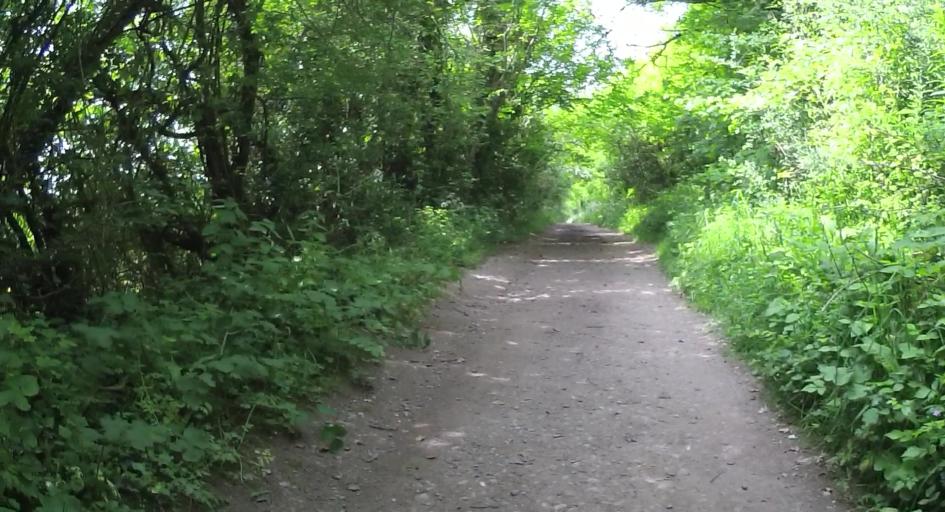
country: GB
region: England
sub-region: Hampshire
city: Kingsclere
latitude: 51.3189
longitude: -1.2340
